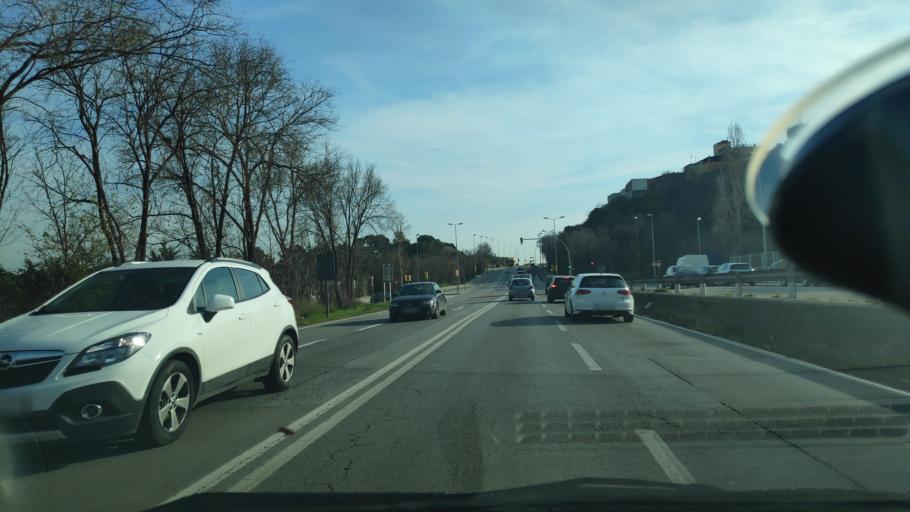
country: ES
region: Catalonia
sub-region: Provincia de Barcelona
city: Sabadell
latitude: 41.5694
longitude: 2.0980
